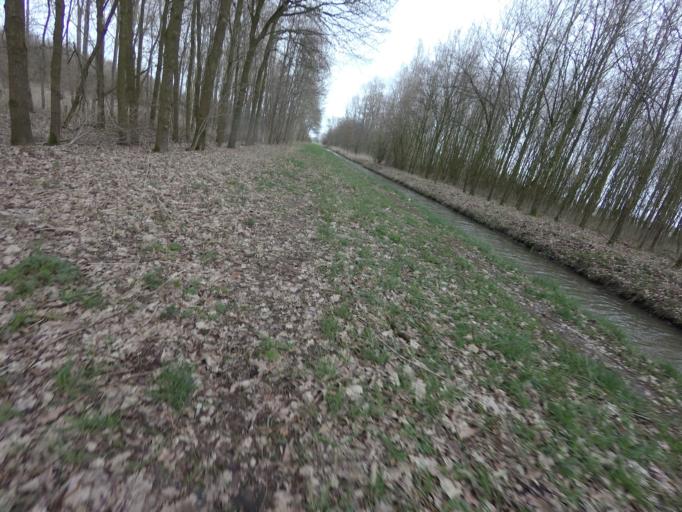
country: NL
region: Utrecht
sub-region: Gemeente IJsselstein
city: IJsselstein
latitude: 52.0382
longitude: 5.0381
